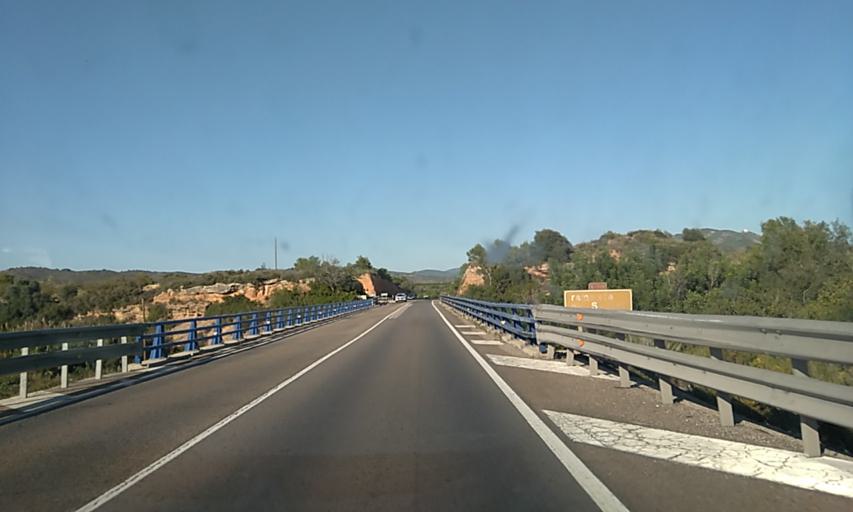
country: ES
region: Valencia
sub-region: Provincia de Castello
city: Torreblanca
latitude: 40.2368
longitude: 0.2235
